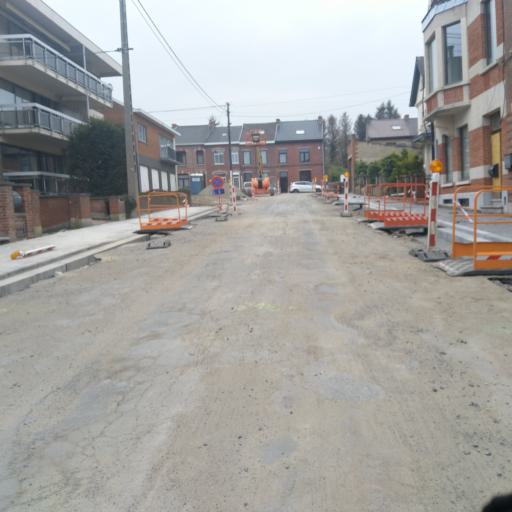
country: BE
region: Wallonia
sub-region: Province du Hainaut
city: Chasse Royale
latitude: 50.4407
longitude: 3.9494
